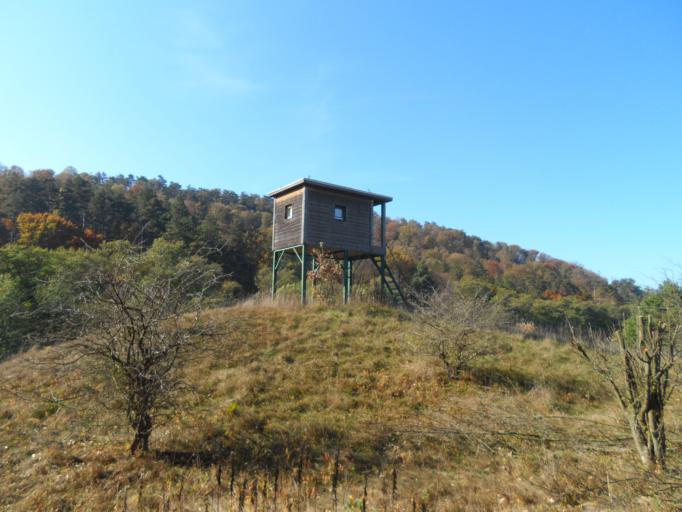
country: HU
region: Veszprem
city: Ajka
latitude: 47.2116
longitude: 17.5723
